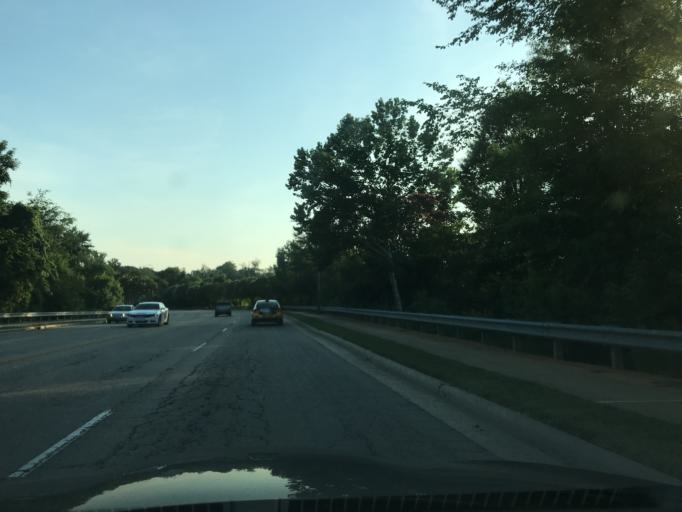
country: US
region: North Carolina
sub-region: Wake County
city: Raleigh
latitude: 35.8066
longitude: -78.6058
